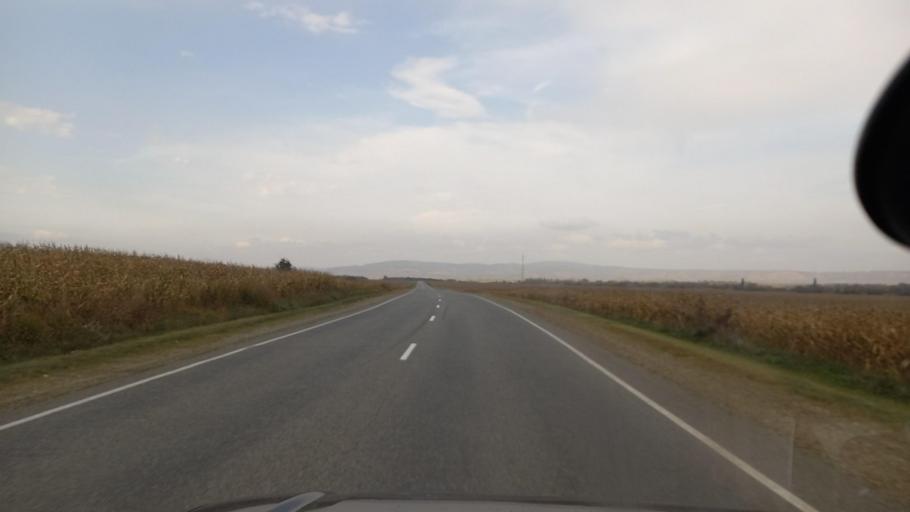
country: RU
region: Krasnodarskiy
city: Shedok
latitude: 44.2541
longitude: 40.8658
